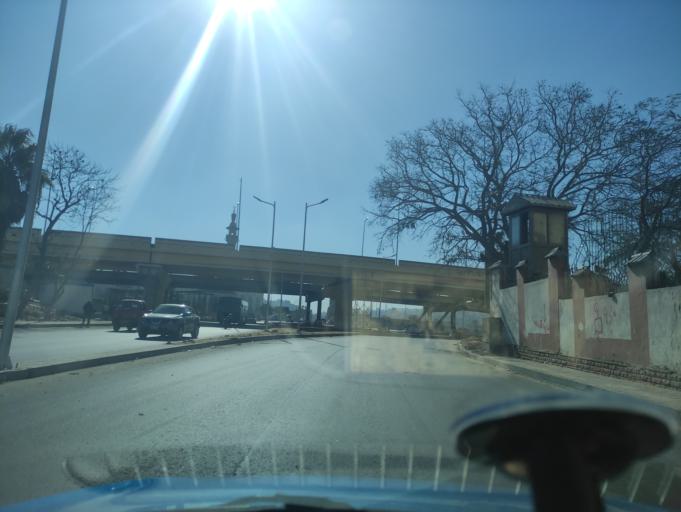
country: EG
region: Muhafazat al Qahirah
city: Cairo
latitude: 30.0562
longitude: 31.2792
